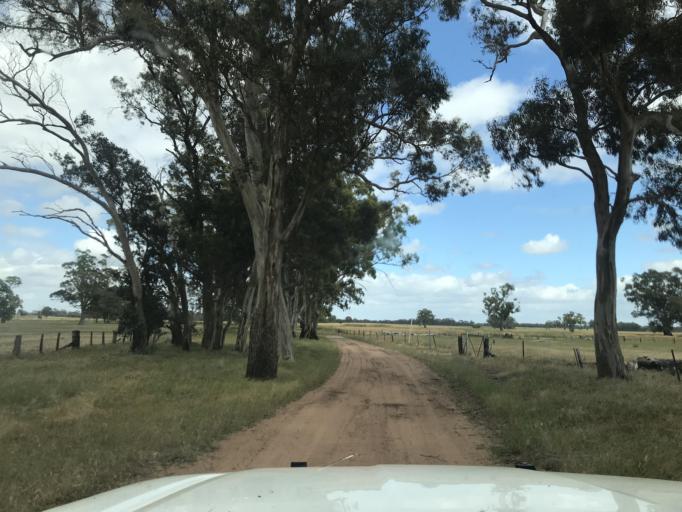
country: AU
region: South Australia
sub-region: Naracoorte and Lucindale
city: Naracoorte
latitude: -36.8990
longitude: 141.3870
